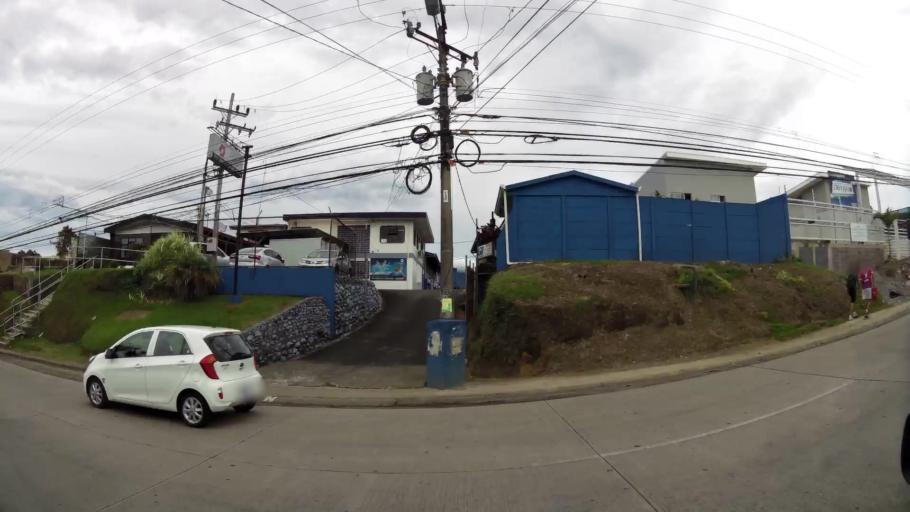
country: CR
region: San Jose
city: Purral
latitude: 9.9658
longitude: -84.0268
